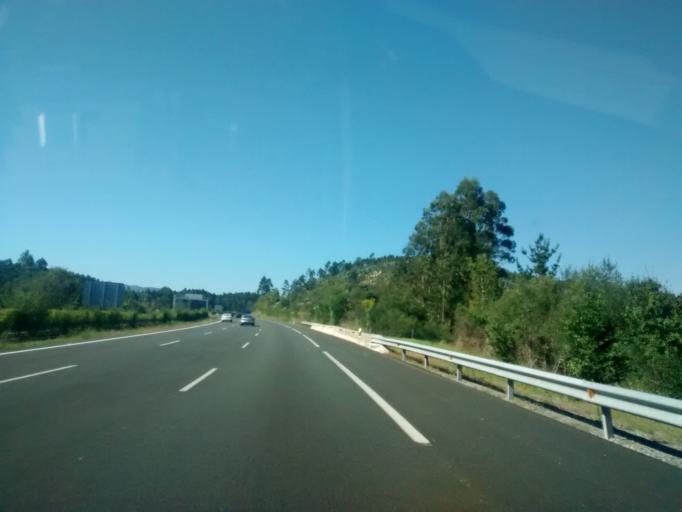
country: ES
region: Cantabria
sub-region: Provincia de Cantabria
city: Luzmela
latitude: 43.3247
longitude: -4.1999
